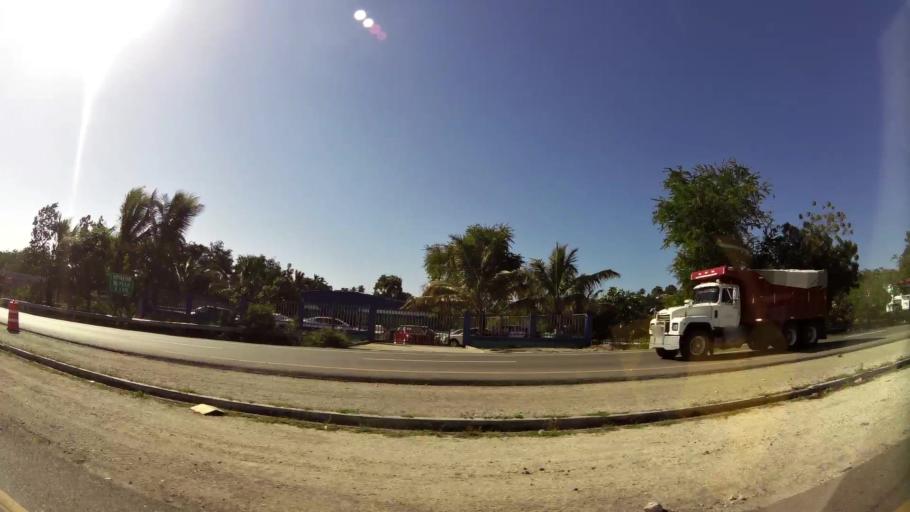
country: DO
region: San Cristobal
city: El Carril
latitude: 18.4376
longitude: -70.0157
